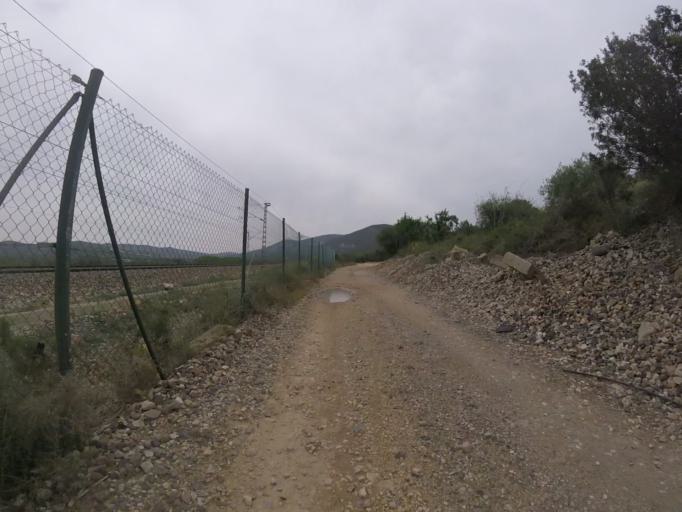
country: ES
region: Valencia
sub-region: Provincia de Castello
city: Alcoceber
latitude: 40.2533
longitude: 0.2506
